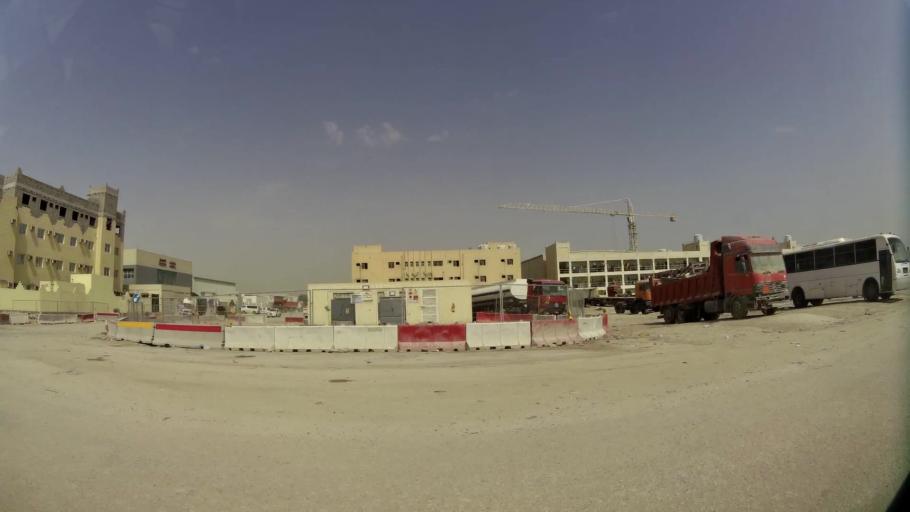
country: QA
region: Al Wakrah
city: Al Wukayr
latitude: 25.1726
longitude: 51.4403
